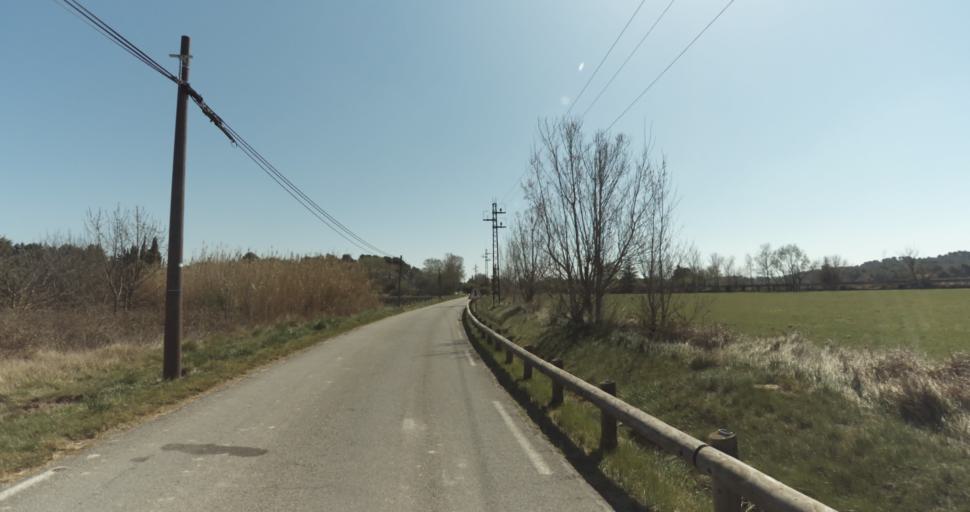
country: FR
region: Provence-Alpes-Cote d'Azur
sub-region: Departement des Bouches-du-Rhone
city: Pelissanne
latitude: 43.6167
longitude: 5.1655
